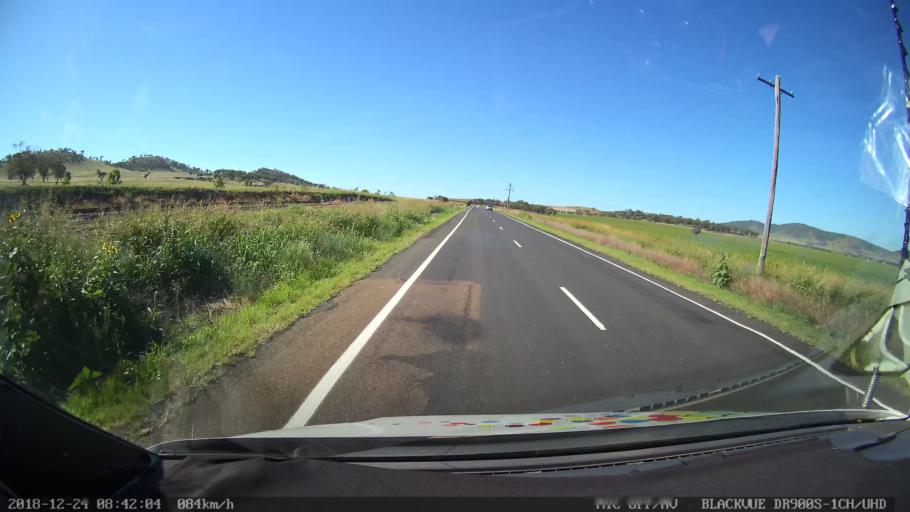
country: AU
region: New South Wales
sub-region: Liverpool Plains
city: Quirindi
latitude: -31.3695
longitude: 150.6437
